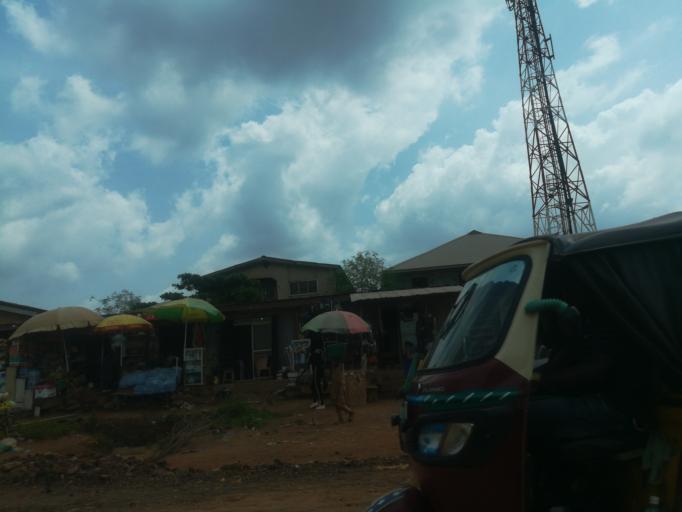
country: NG
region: Oyo
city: Ibadan
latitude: 7.4371
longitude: 3.9468
